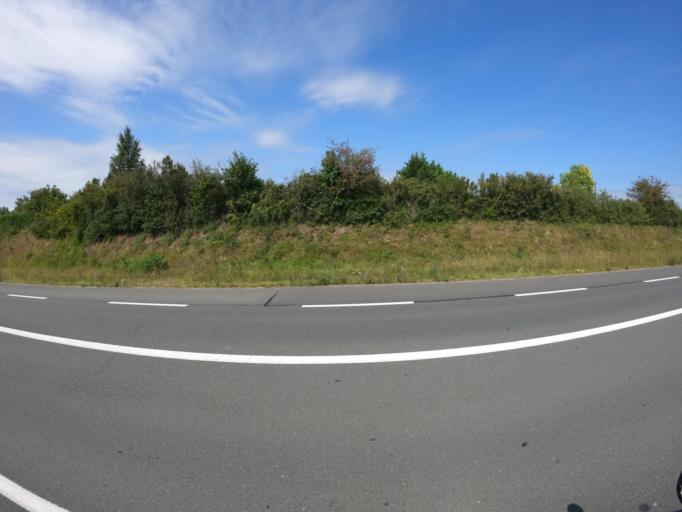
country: FR
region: Poitou-Charentes
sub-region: Departement des Deux-Sevres
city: Mauze-sur-le-Mignon
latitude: 46.1943
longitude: -0.6610
